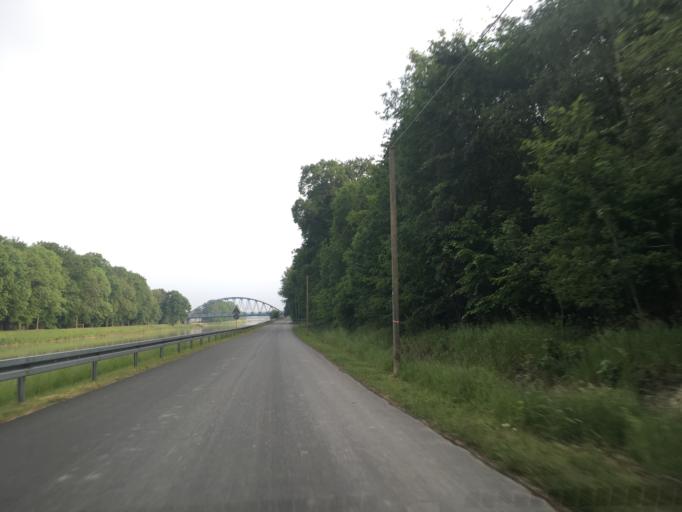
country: DE
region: North Rhine-Westphalia
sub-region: Regierungsbezirk Munster
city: Muenster
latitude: 51.9992
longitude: 7.6588
